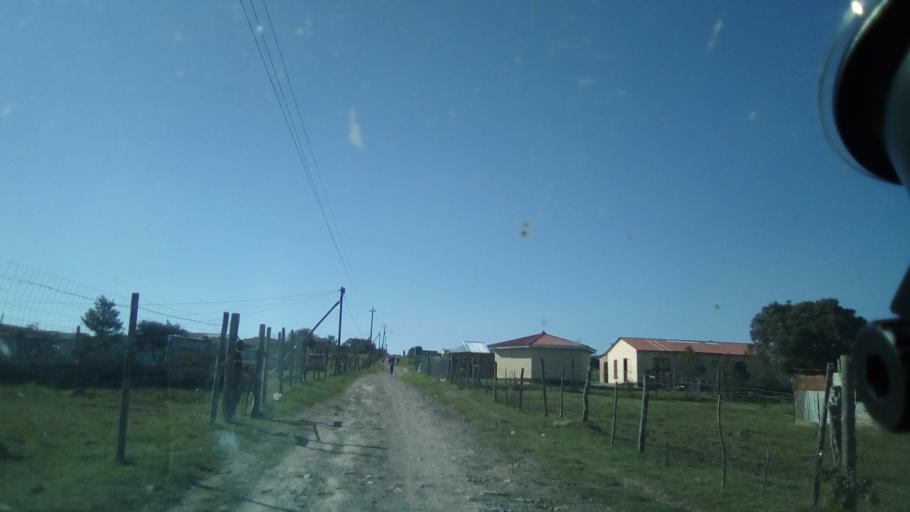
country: ZA
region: Eastern Cape
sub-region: Buffalo City Metropolitan Municipality
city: Bhisho
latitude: -32.8289
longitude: 27.3690
